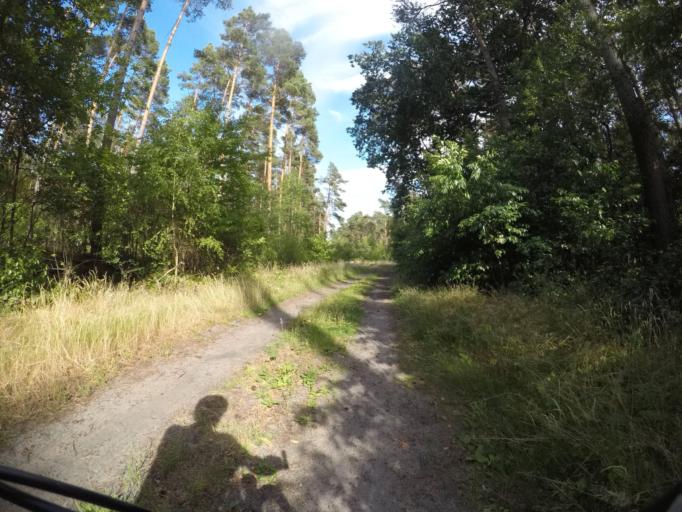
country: DE
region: Lower Saxony
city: Neu Darchau
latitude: 53.2795
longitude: 10.9444
